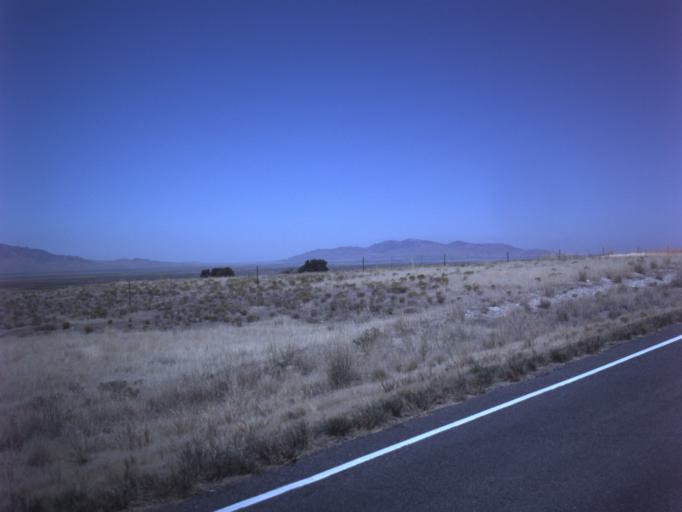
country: US
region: Utah
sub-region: Tooele County
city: Grantsville
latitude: 40.5835
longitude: -112.7241
